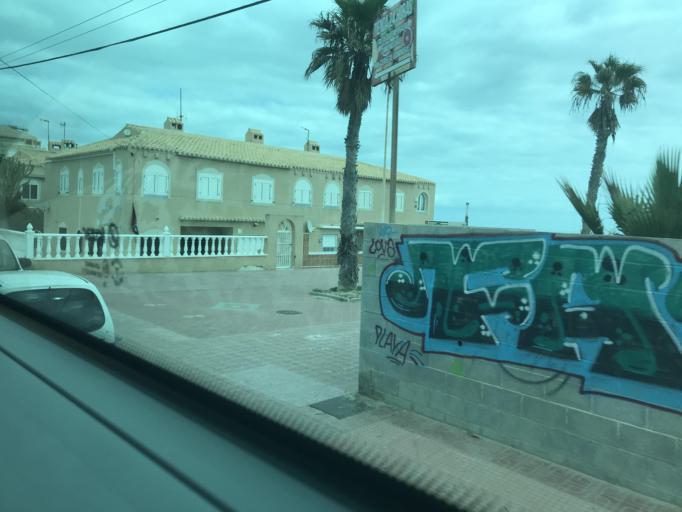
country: ES
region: Valencia
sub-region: Provincia de Alicante
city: Torrevieja
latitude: 38.0234
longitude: -0.6542
